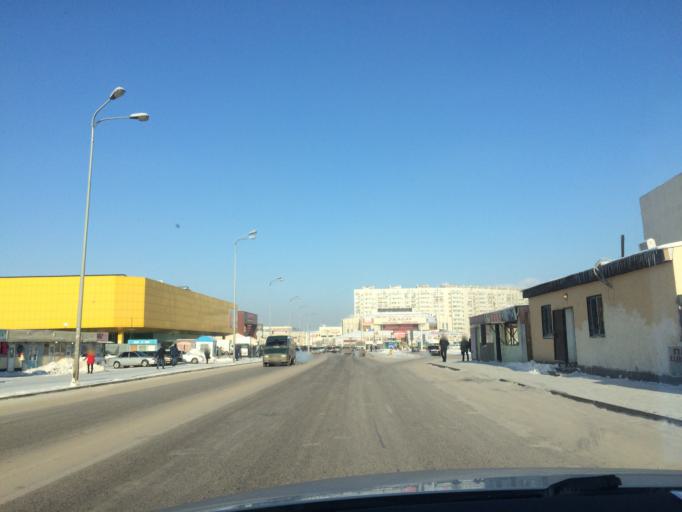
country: KZ
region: Astana Qalasy
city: Astana
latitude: 51.1769
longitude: 71.4372
